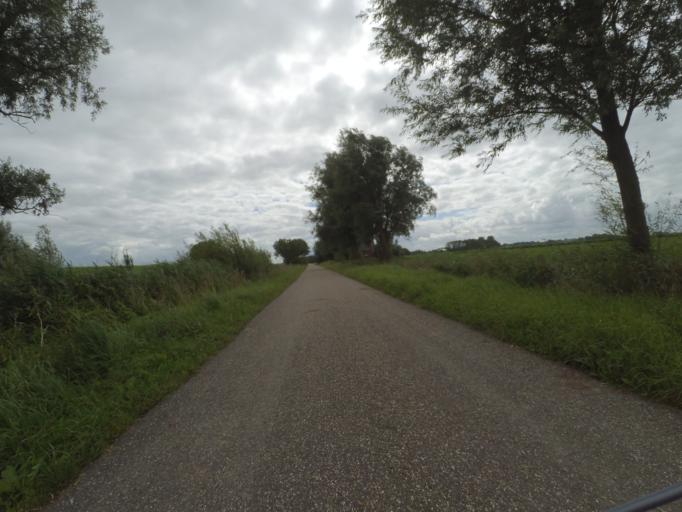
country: NL
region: Friesland
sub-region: Gemeente Dongeradeel
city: Anjum
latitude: 53.3357
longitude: 6.1535
